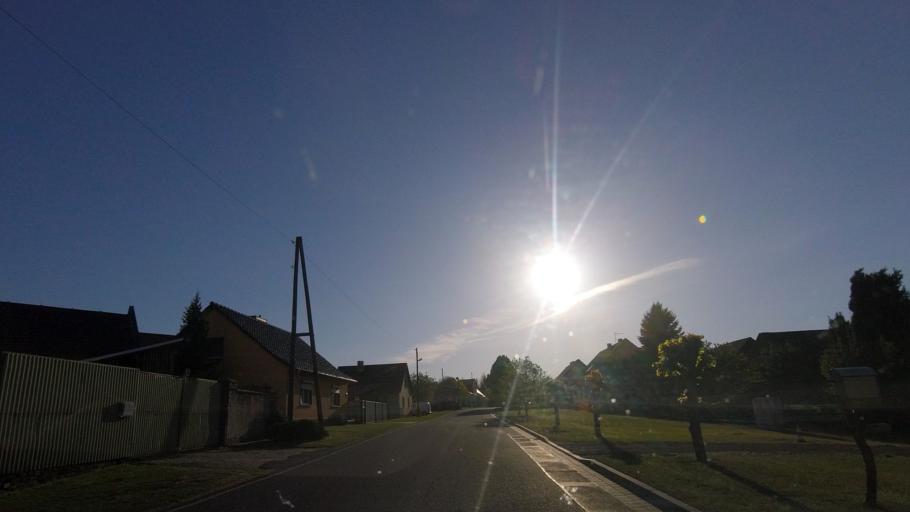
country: DE
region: Brandenburg
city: Baruth
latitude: 52.0000
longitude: 13.4211
